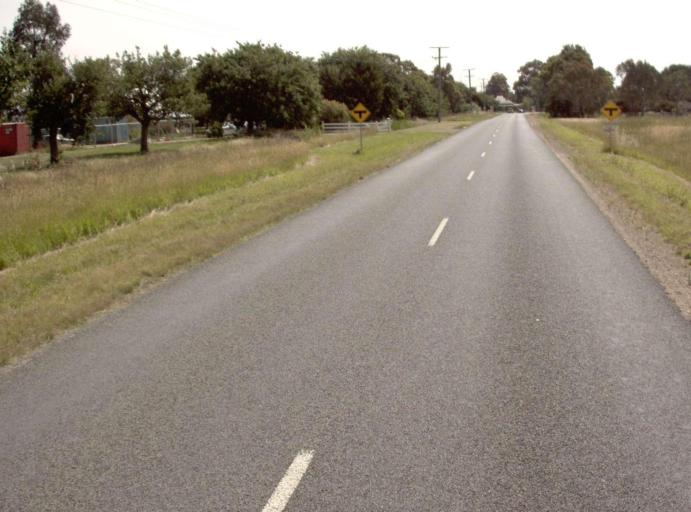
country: AU
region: Victoria
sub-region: Wellington
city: Heyfield
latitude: -38.1542
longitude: 146.7930
